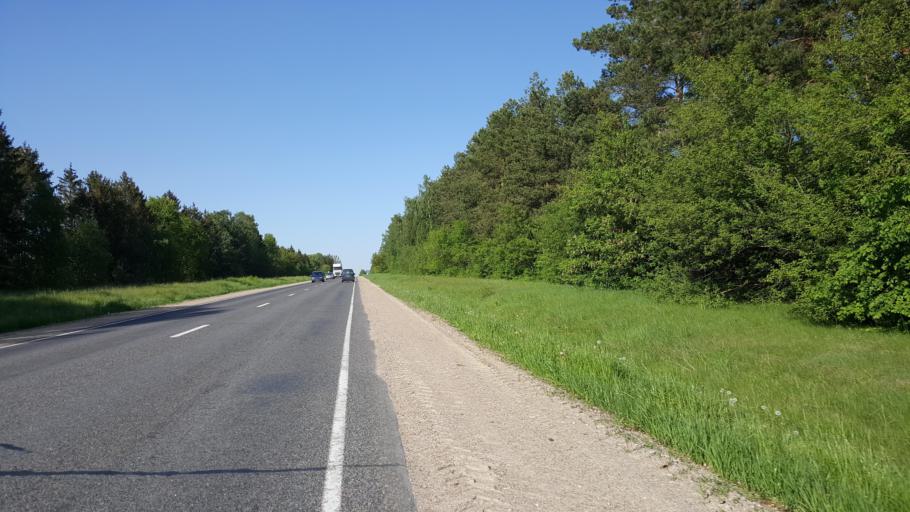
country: BY
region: Brest
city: Kamyanyets
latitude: 52.3635
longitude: 23.7836
